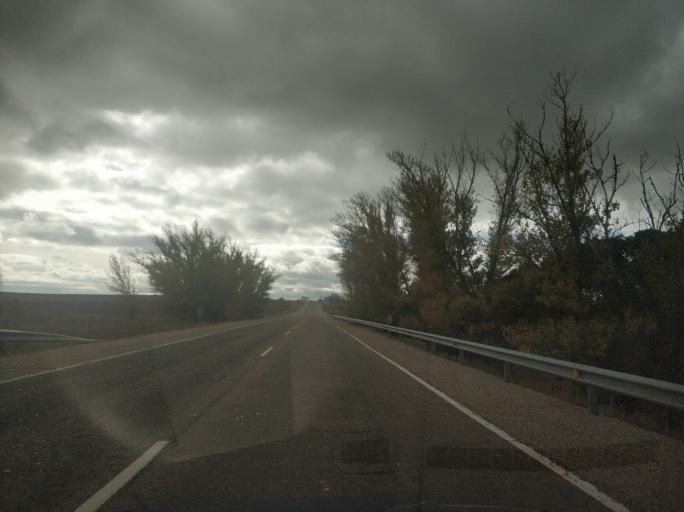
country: ES
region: Castille and Leon
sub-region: Provincia de Zamora
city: Castrillo de la Guarena
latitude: 41.2286
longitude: -5.3118
